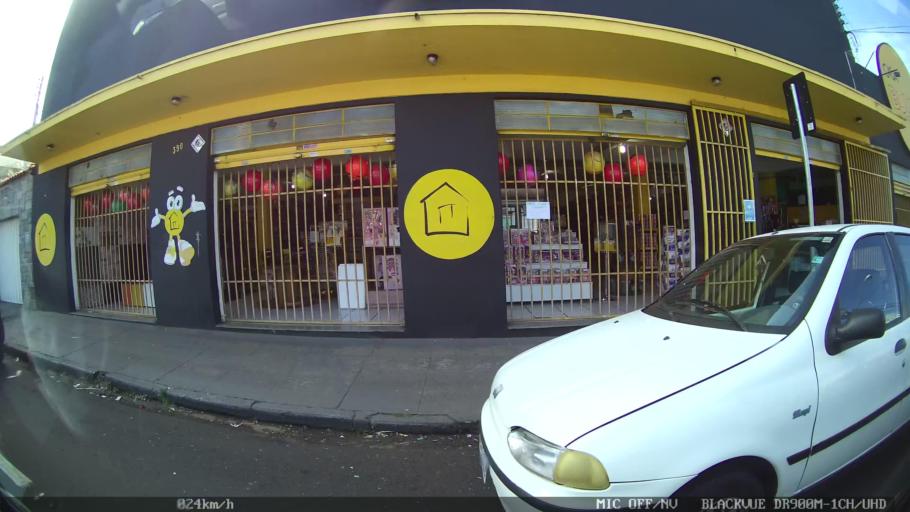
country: BR
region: Sao Paulo
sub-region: Franca
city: Franca
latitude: -20.5334
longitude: -47.4156
